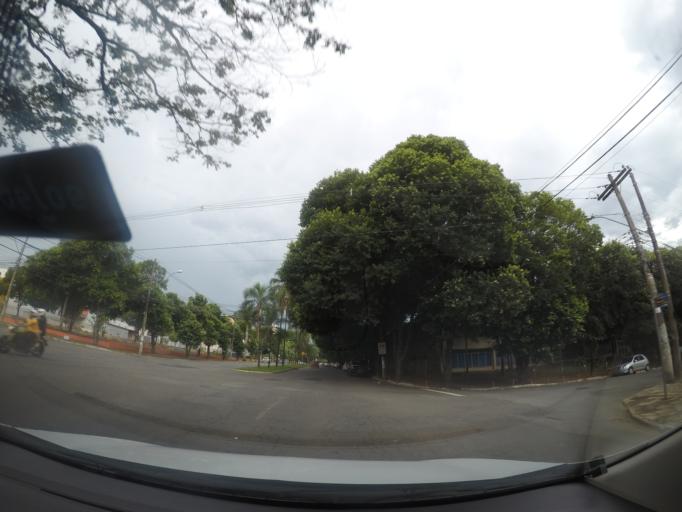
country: BR
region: Goias
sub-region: Goiania
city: Goiania
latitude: -16.6742
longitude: -49.2436
